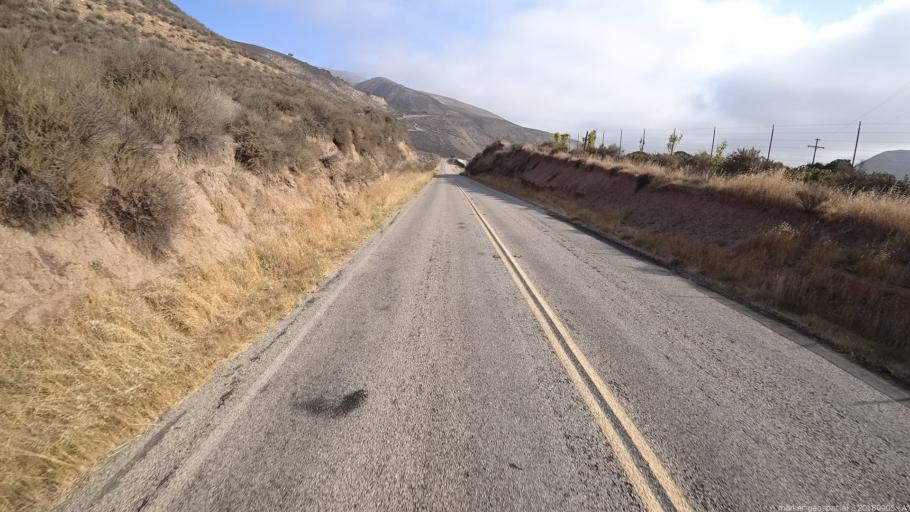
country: US
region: California
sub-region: Monterey County
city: Greenfield
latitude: 36.2718
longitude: -121.3339
